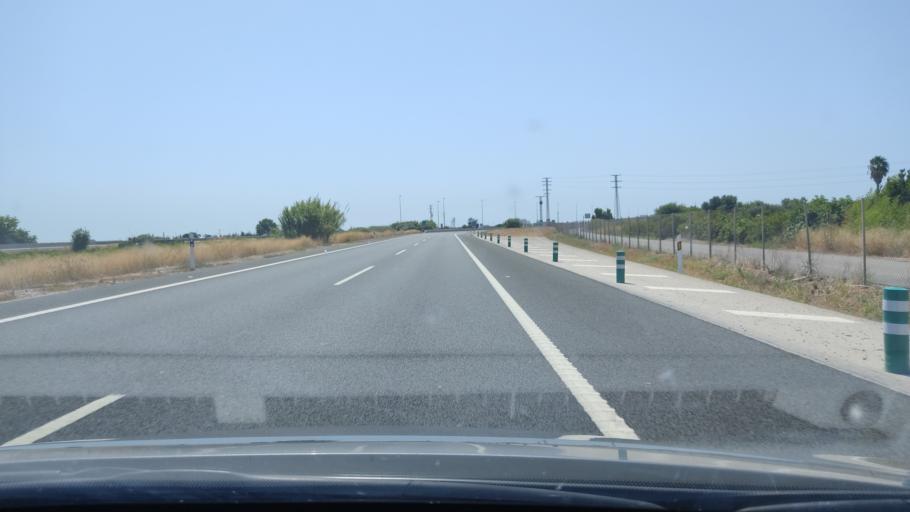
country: ES
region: Valencia
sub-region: Provincia de Valencia
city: Pucol
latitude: 39.6218
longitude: -0.2969
